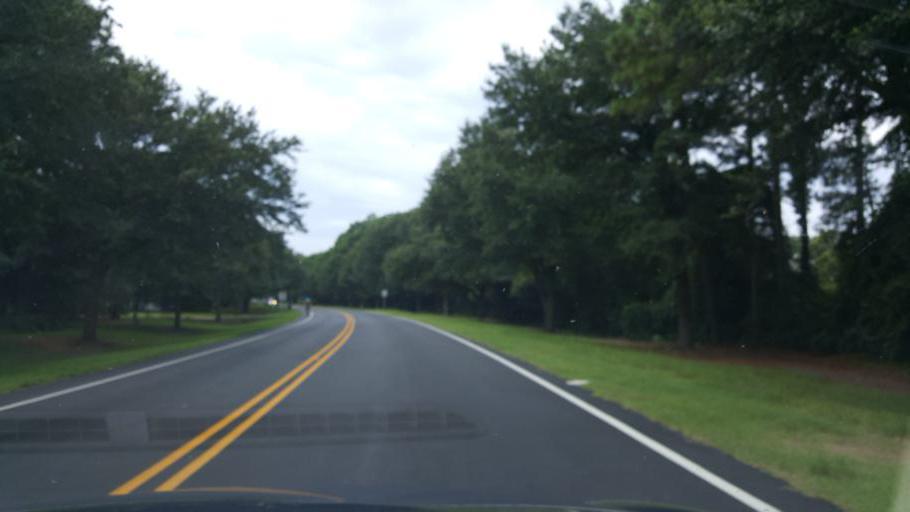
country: US
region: North Carolina
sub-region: Dare County
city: Manteo
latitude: 35.9341
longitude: -75.7030
